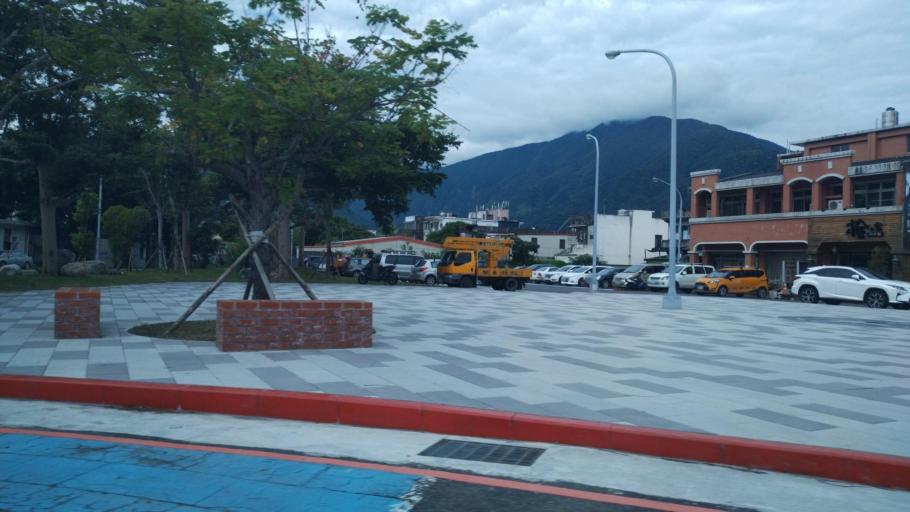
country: TW
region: Taiwan
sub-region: Yilan
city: Yilan
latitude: 24.4638
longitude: 121.8008
